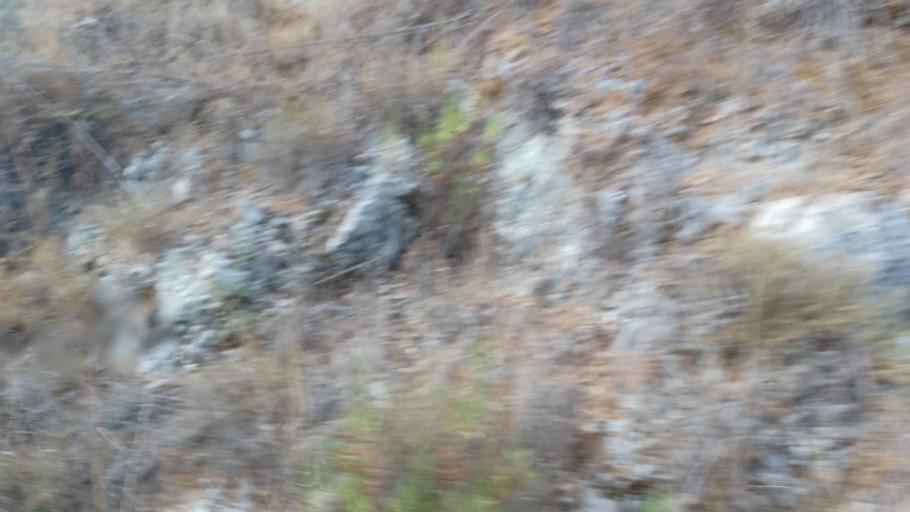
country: CY
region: Pafos
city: Tala
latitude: 34.9122
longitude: 32.4982
